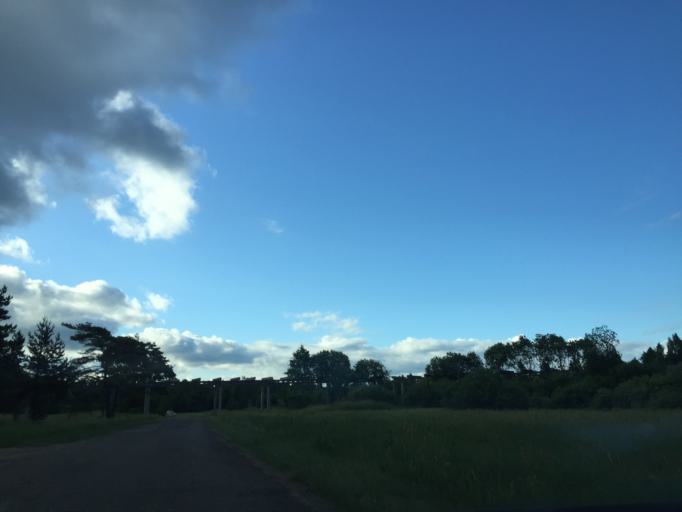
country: LV
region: Ventspils
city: Ventspils
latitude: 57.4106
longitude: 21.6162
